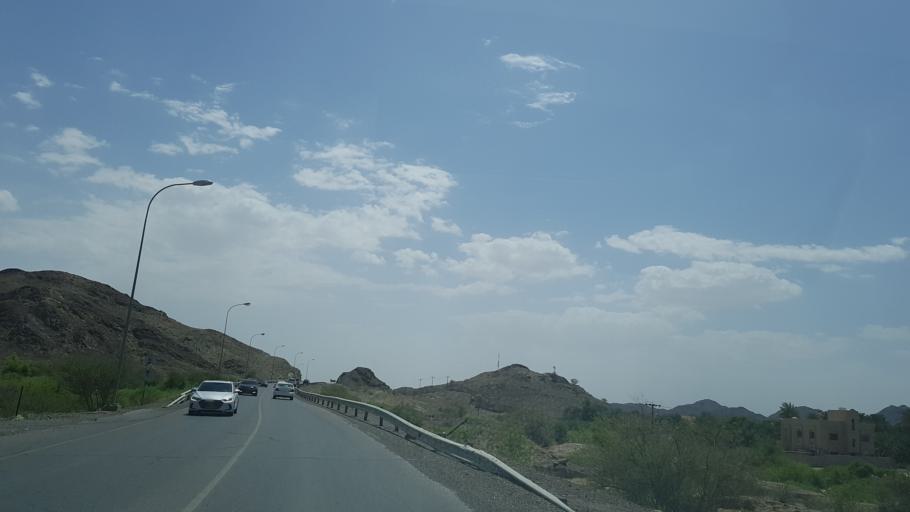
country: OM
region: Muhafazat ad Dakhiliyah
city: Bahla'
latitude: 22.9746
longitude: 57.3034
